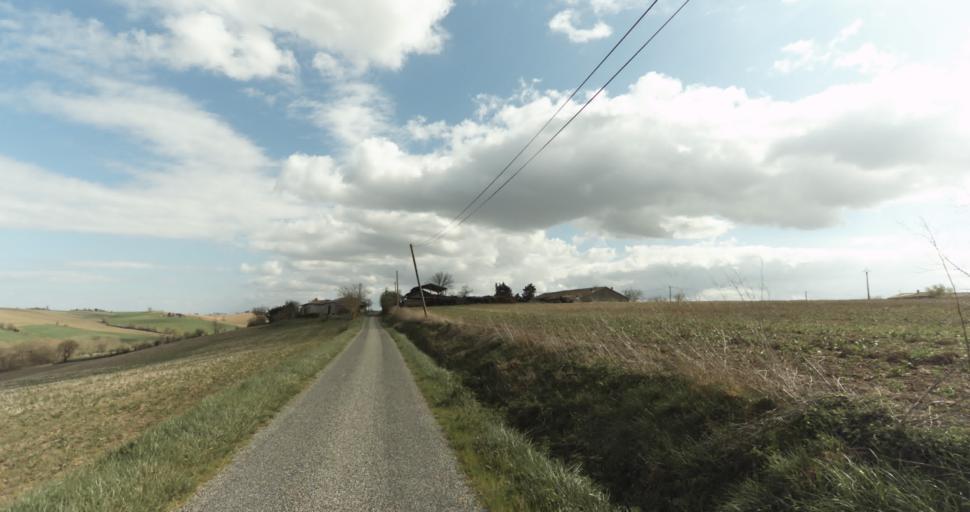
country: FR
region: Midi-Pyrenees
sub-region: Departement de la Haute-Garonne
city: Auterive
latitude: 43.3710
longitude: 1.4856
